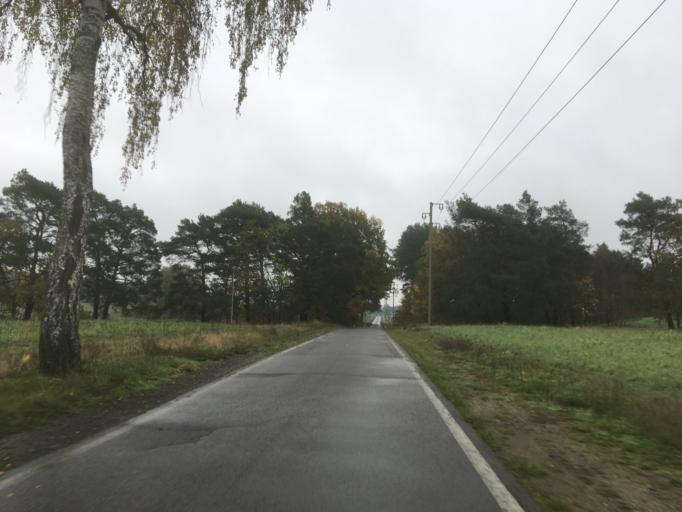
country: DE
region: Brandenburg
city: Neu Zauche
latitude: 52.0351
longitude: 14.0615
